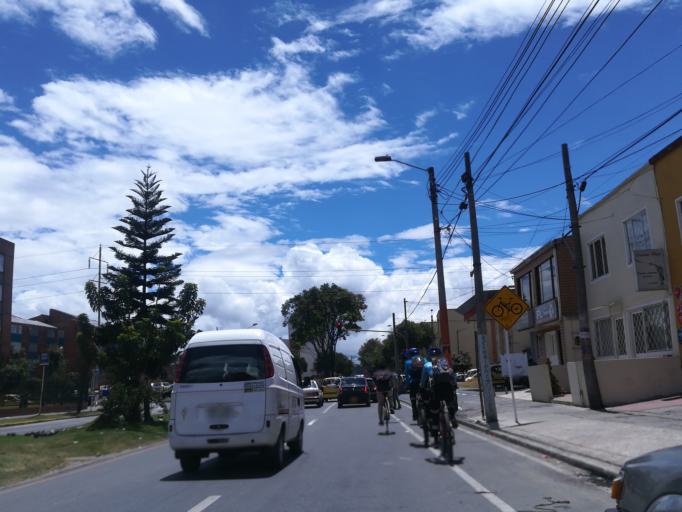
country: CO
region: Bogota D.C.
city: Bogota
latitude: 4.6144
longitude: -74.1503
